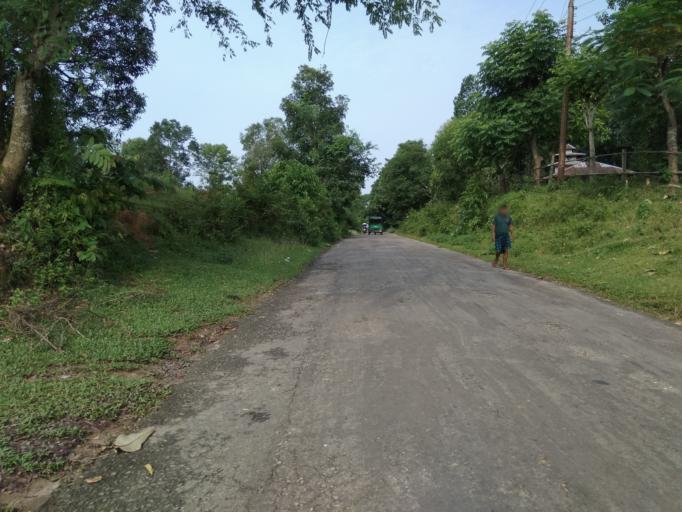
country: BD
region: Chittagong
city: Khagrachhari
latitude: 23.0112
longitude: 92.0127
